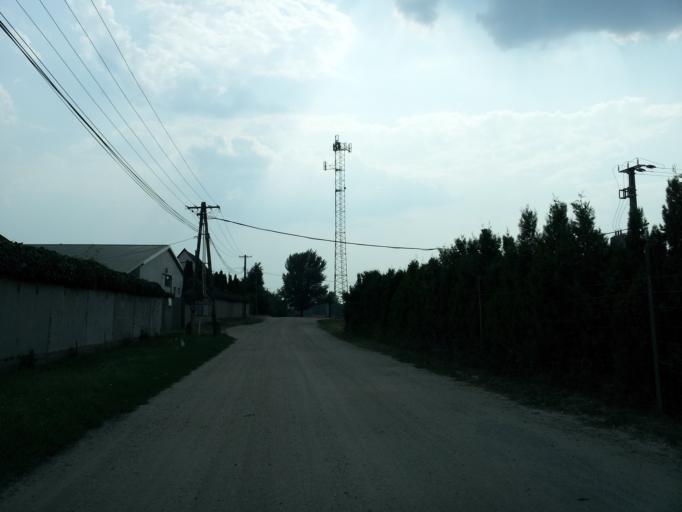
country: HU
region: Gyor-Moson-Sopron
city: Gyorujbarat
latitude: 47.6433
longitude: 17.6766
